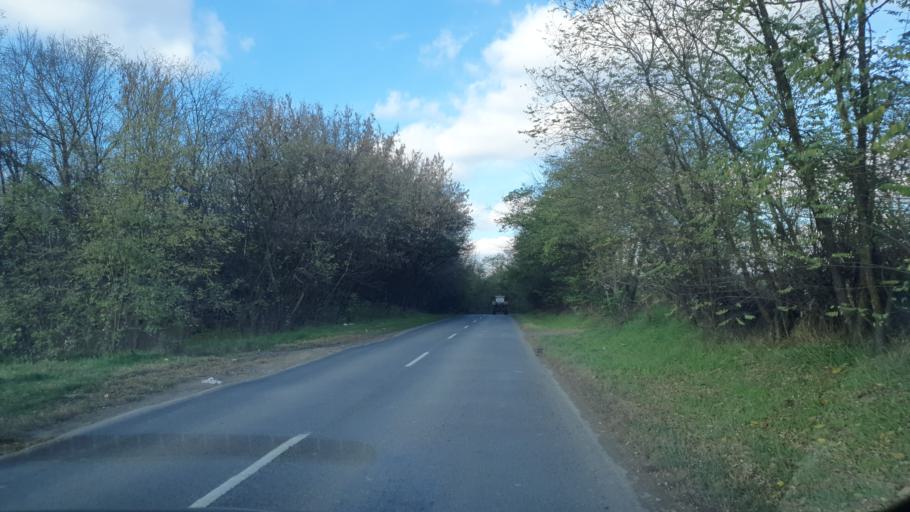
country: HU
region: Szabolcs-Szatmar-Bereg
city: Anarcs
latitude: 48.1651
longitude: 22.0968
